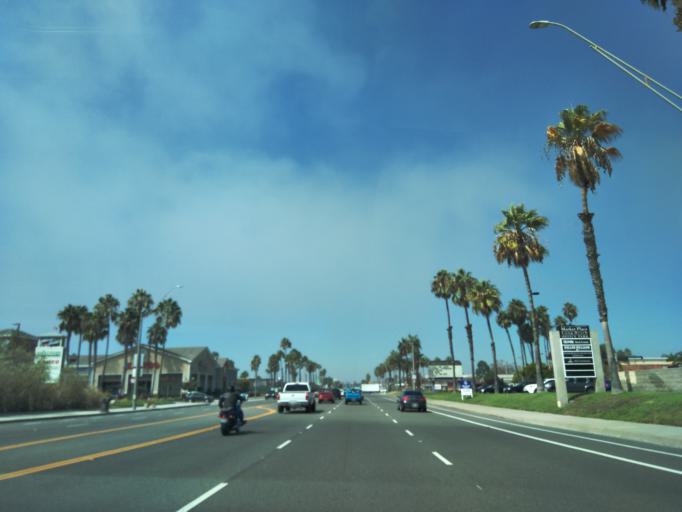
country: US
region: California
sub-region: Orange County
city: Seal Beach
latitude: 33.7545
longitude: -118.1077
